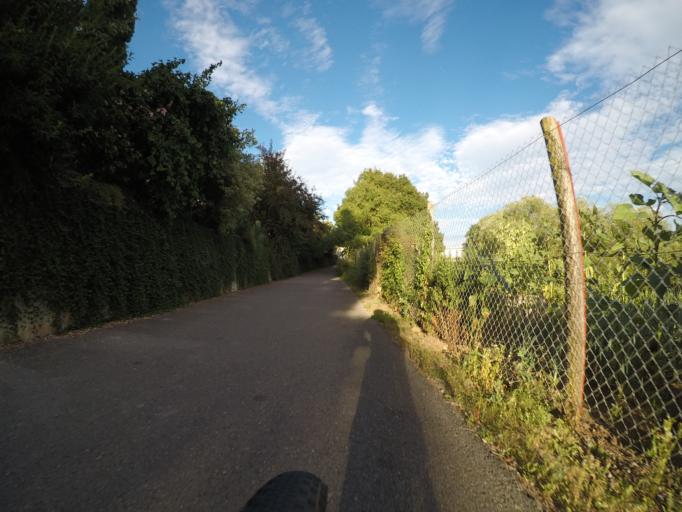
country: DE
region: Baden-Wuerttemberg
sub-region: Regierungsbezirk Stuttgart
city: Ehningen
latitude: 48.6917
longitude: 8.9586
